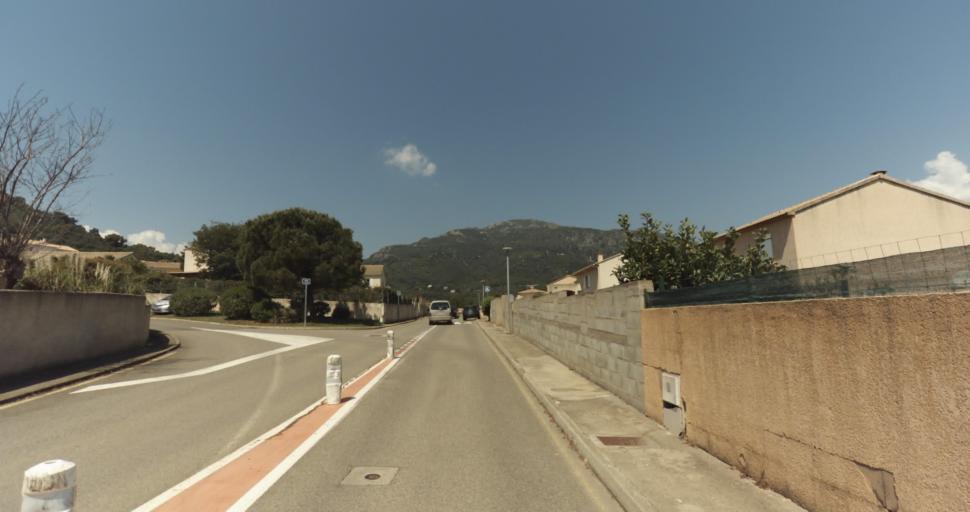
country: FR
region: Corsica
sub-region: Departement de la Haute-Corse
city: Biguglia
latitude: 42.6066
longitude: 9.4309
